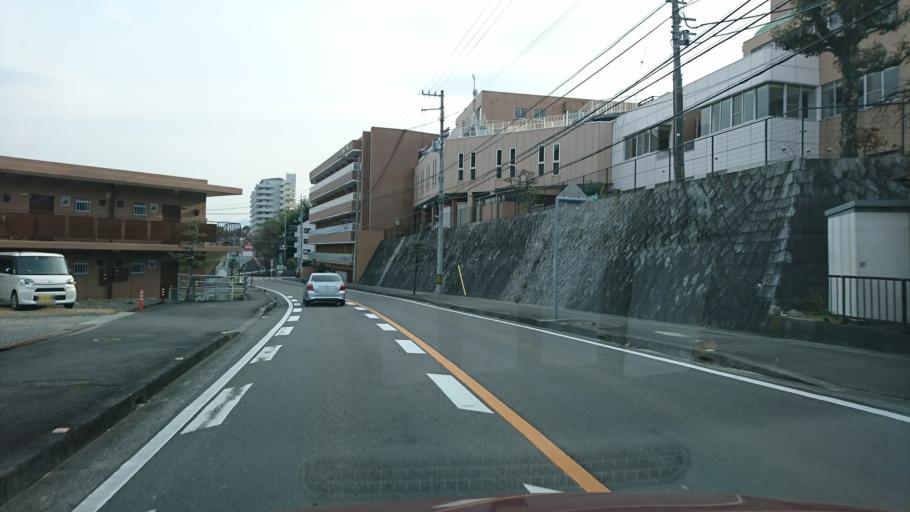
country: JP
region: Ehime
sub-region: Shikoku-chuo Shi
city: Matsuyama
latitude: 33.8646
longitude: 132.7734
